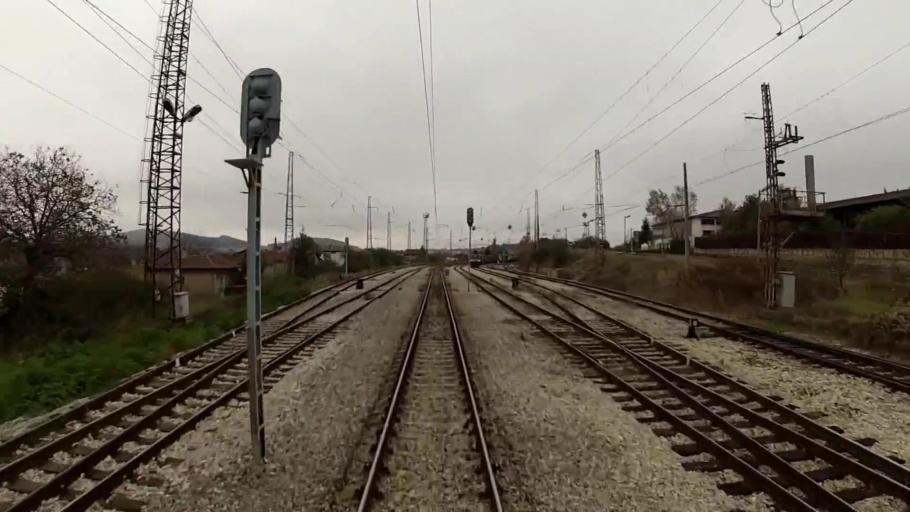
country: BG
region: Sofiya
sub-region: Obshtina Dragoman
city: Dragoman
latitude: 42.9297
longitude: 22.9300
